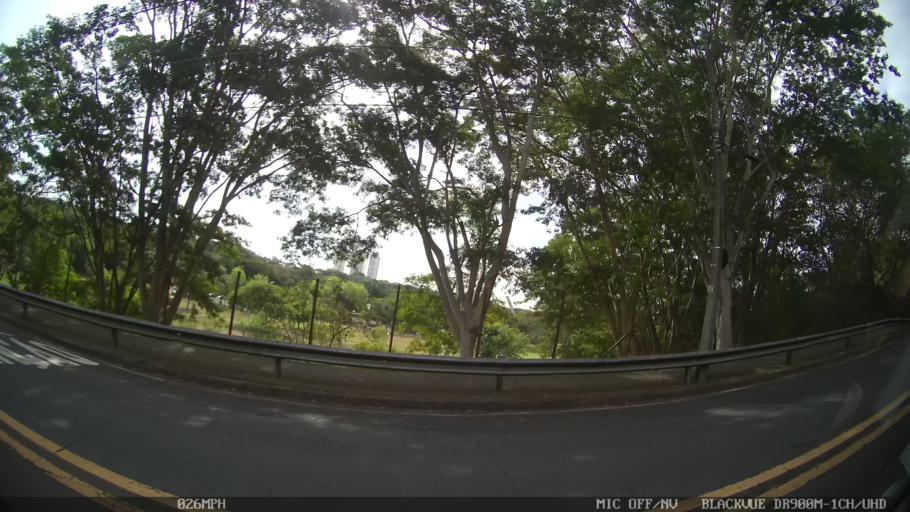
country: BR
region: Sao Paulo
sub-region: Piracicaba
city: Piracicaba
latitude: -22.7273
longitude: -47.6599
